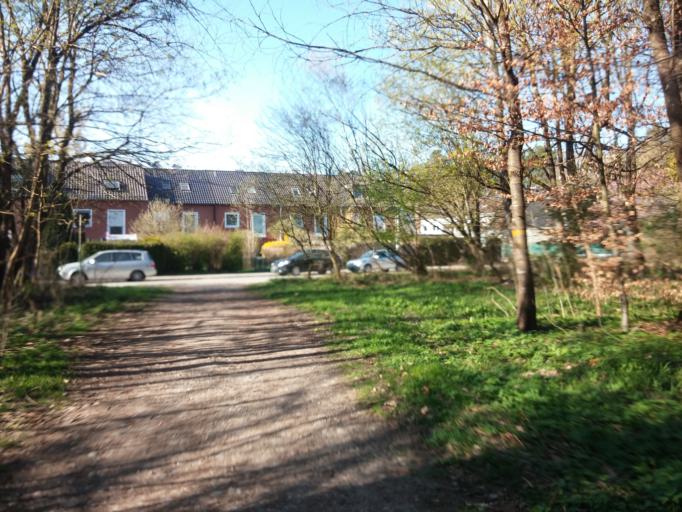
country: DE
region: Bavaria
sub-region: Upper Bavaria
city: Neubiberg
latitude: 48.1051
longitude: 11.6774
